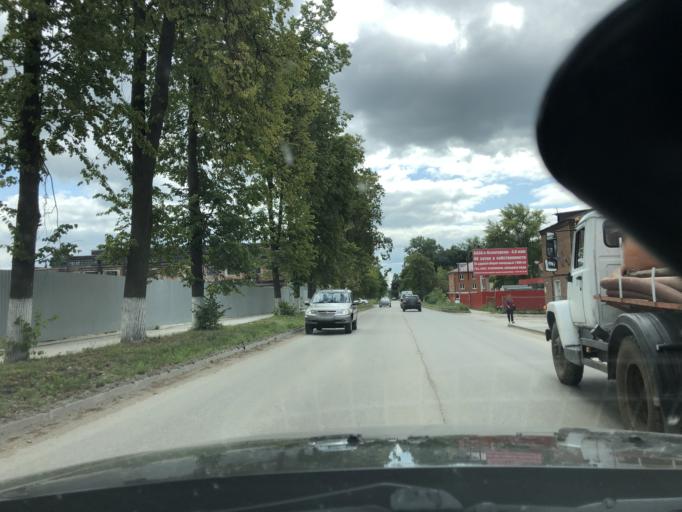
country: RU
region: Tula
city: Yasnogorsk
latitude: 54.4762
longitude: 37.6978
